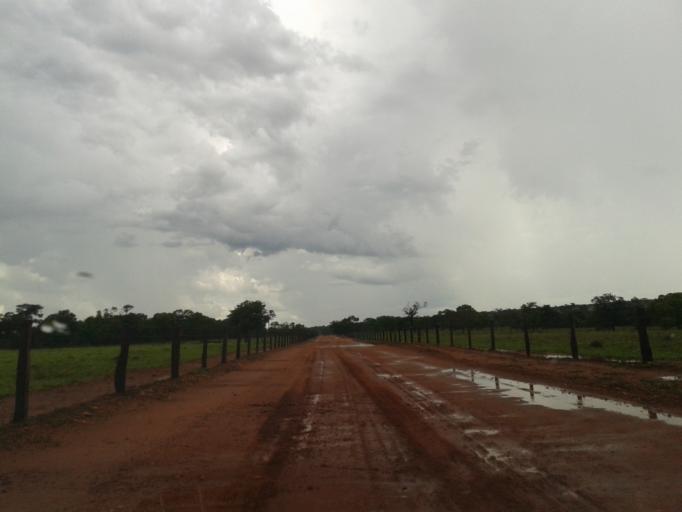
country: BR
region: Minas Gerais
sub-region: Santa Vitoria
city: Santa Vitoria
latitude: -19.1489
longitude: -50.5635
